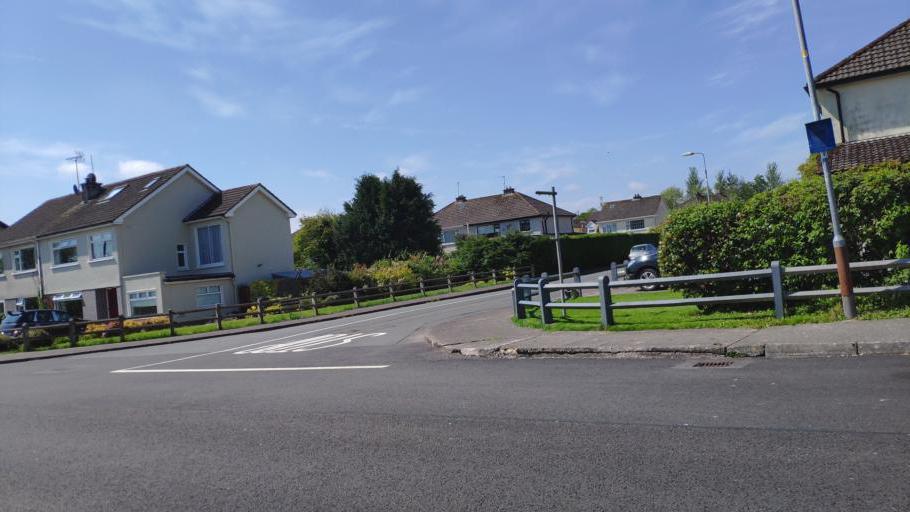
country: IE
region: Munster
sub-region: County Cork
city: Blarney
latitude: 51.9306
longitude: -8.5590
